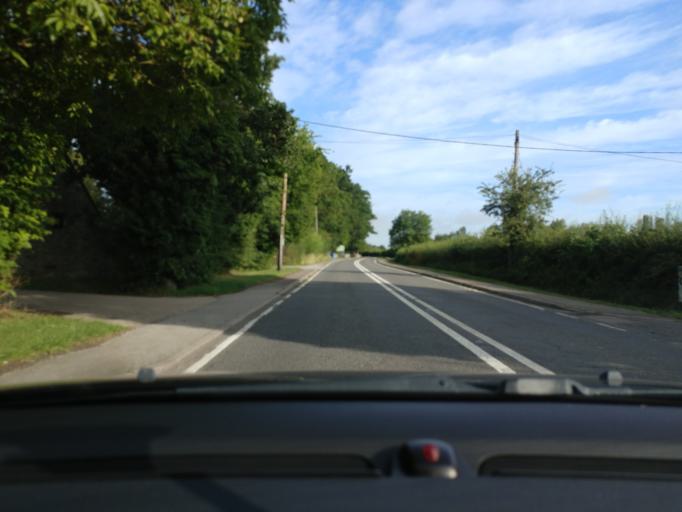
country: GB
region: England
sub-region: Oxfordshire
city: Kidlington
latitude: 51.8610
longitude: -1.2234
